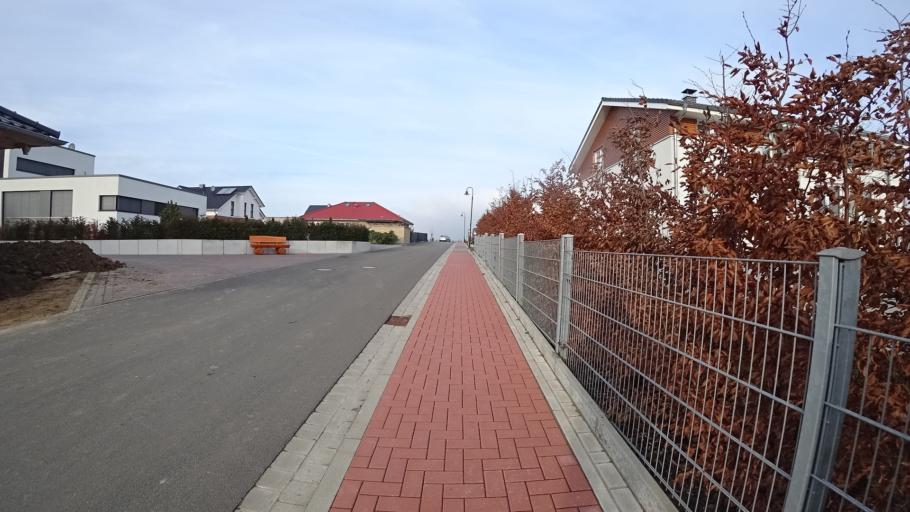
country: DE
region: Lower Saxony
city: Lauenau
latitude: 52.2788
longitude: 9.3790
